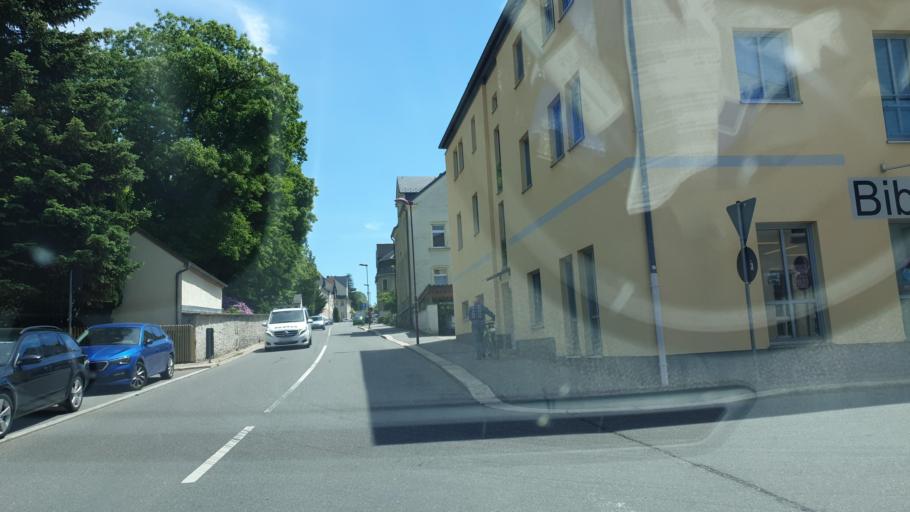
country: DE
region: Saxony
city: Rodewisch
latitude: 50.5304
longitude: 12.4061
